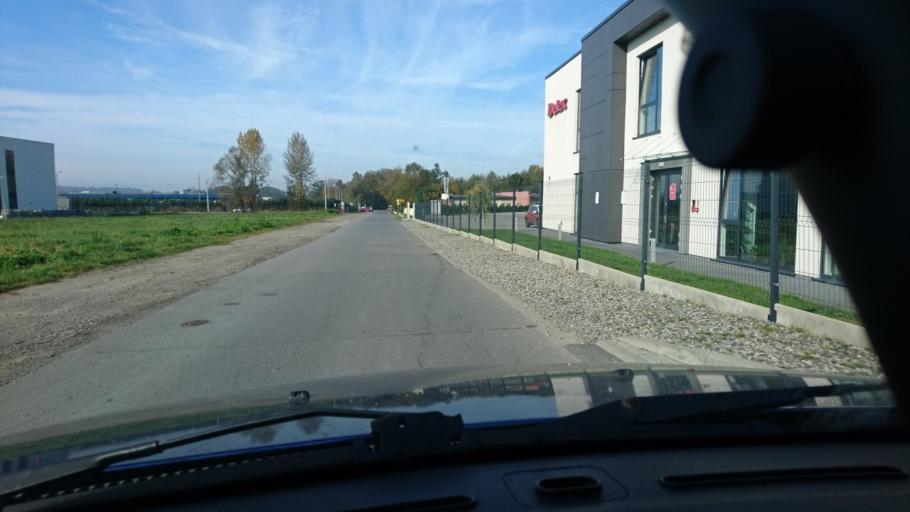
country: PL
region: Silesian Voivodeship
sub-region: Powiat bielski
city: Mazancowice
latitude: 49.8232
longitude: 18.9803
